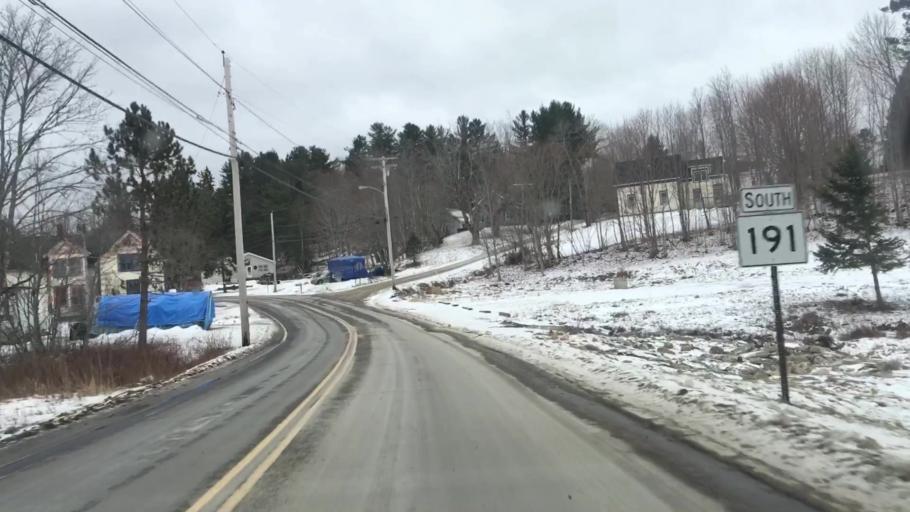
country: US
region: Maine
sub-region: Washington County
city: East Machias
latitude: 44.7318
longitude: -67.3906
